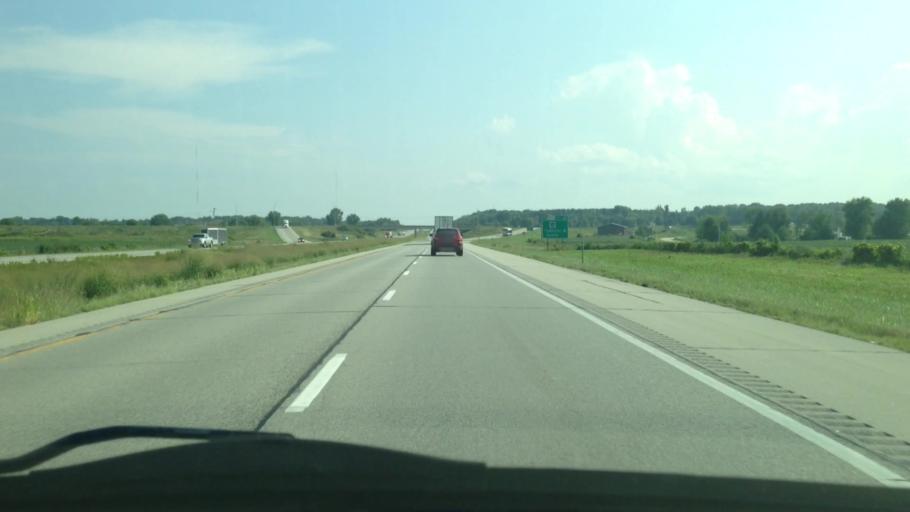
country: US
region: Iowa
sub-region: Linn County
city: Robins
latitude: 42.0985
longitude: -91.7019
